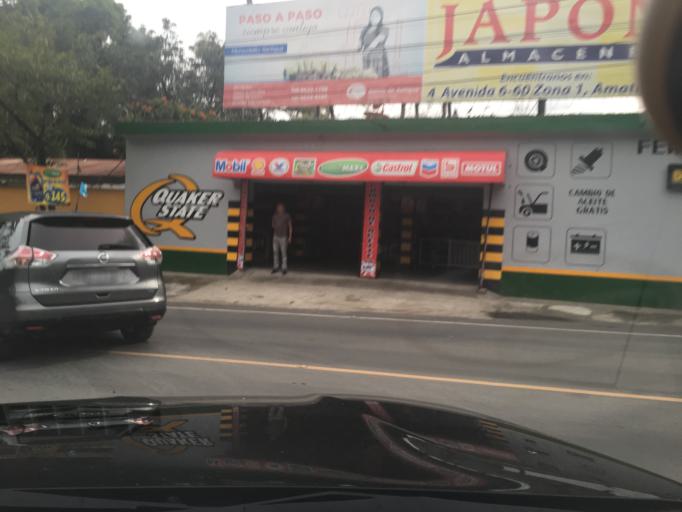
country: GT
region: Guatemala
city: Amatitlan
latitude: 14.4856
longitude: -90.6179
